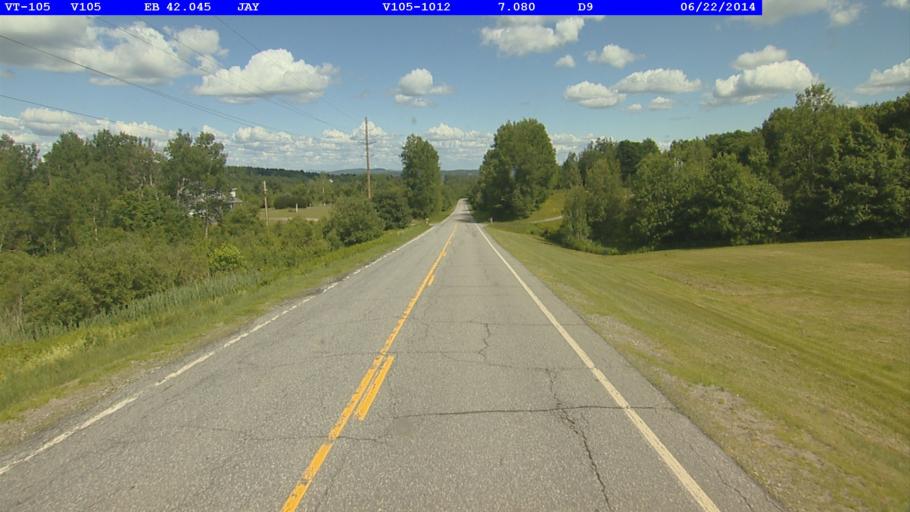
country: CA
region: Quebec
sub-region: Monteregie
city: Sutton
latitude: 44.9696
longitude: -72.4470
